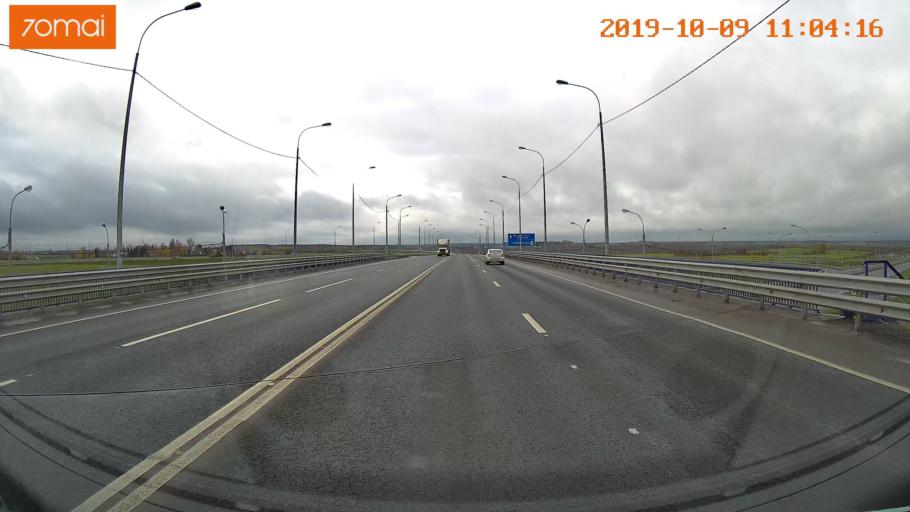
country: RU
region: Vologda
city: Vologda
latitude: 59.2139
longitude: 39.7693
